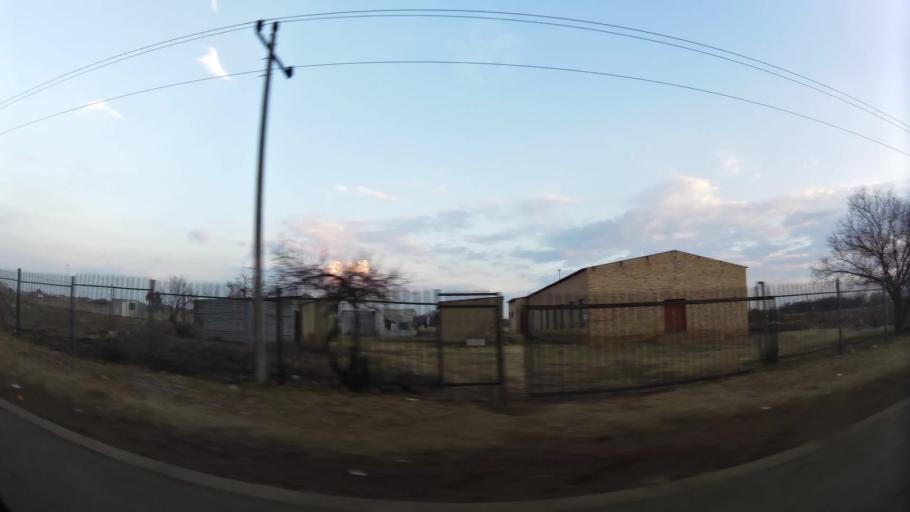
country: ZA
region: Gauteng
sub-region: City of Johannesburg Metropolitan Municipality
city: Orange Farm
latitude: -26.5463
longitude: 27.8769
